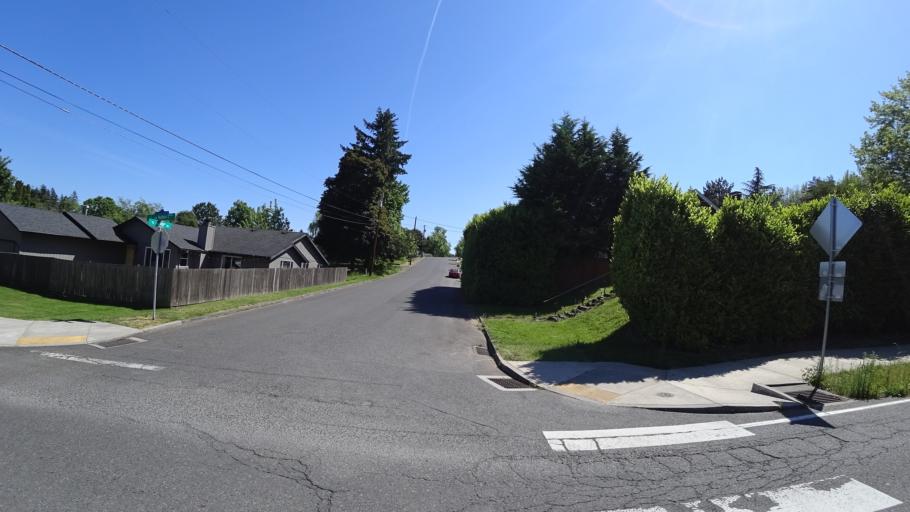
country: US
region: Oregon
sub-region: Washington County
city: Metzger
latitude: 45.4522
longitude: -122.7180
